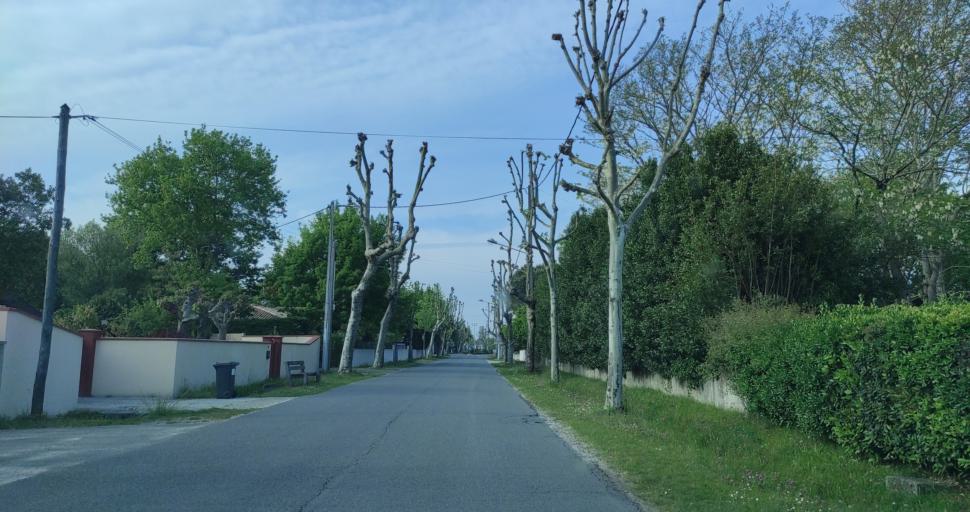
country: FR
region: Aquitaine
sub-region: Departement de la Gironde
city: Ares
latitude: 44.7593
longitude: -1.1329
